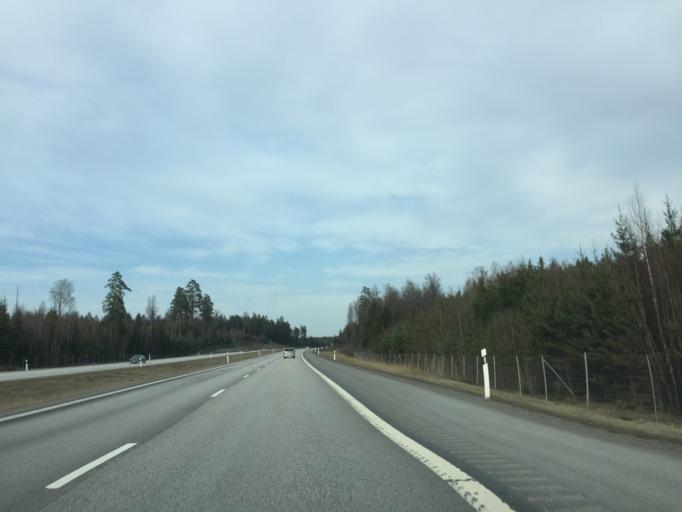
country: SE
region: OErebro
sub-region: Lindesbergs Kommun
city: Fellingsbro
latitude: 59.3634
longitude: 15.5736
